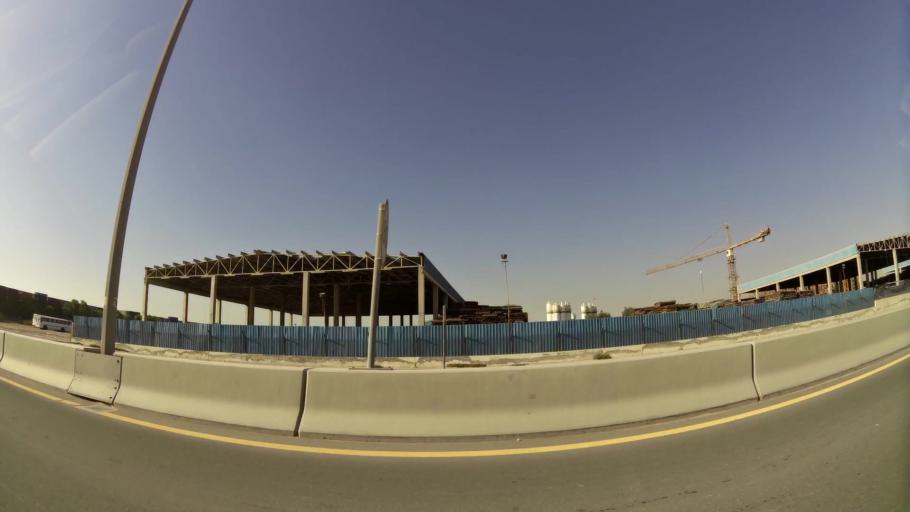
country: AE
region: Dubai
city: Dubai
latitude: 24.9892
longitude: 55.1120
